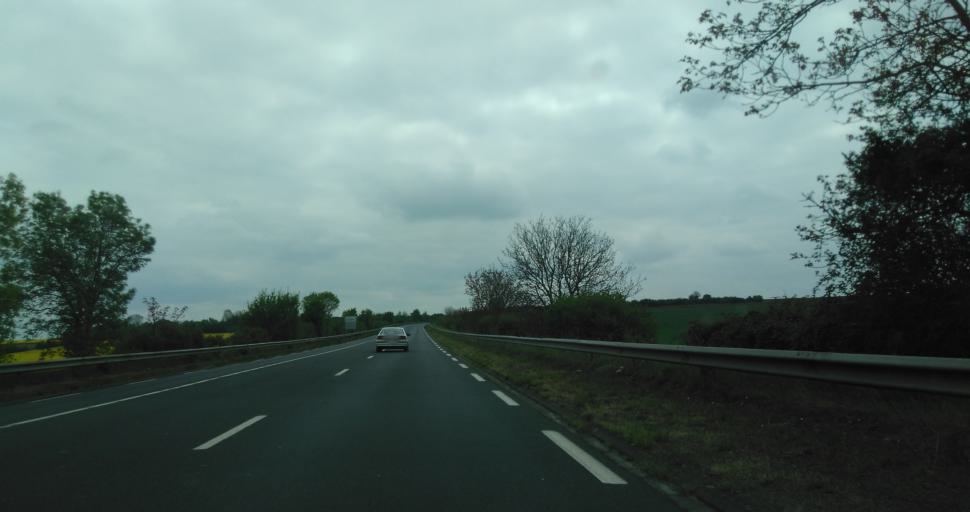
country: FR
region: Poitou-Charentes
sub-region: Departement des Deux-Sevres
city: Echire
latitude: 46.3777
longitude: -0.4274
